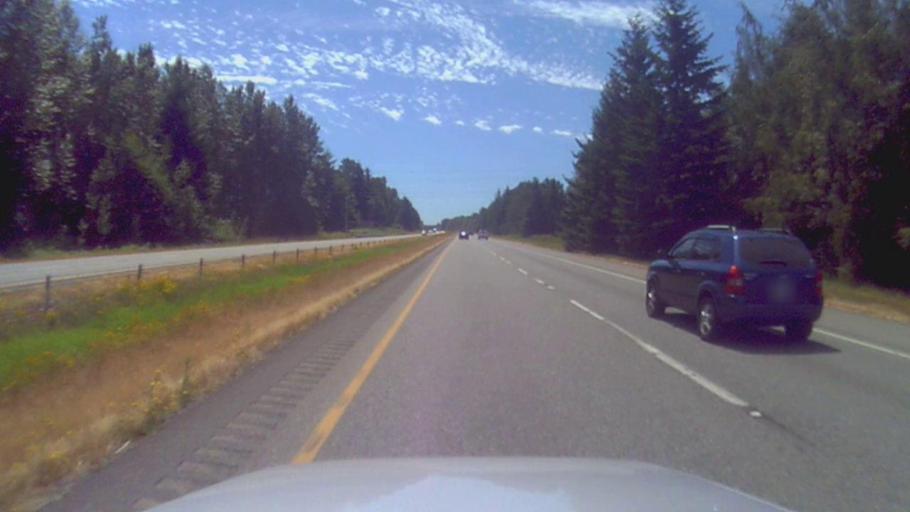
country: US
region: Washington
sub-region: Whatcom County
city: Ferndale
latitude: 48.8789
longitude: -122.5890
